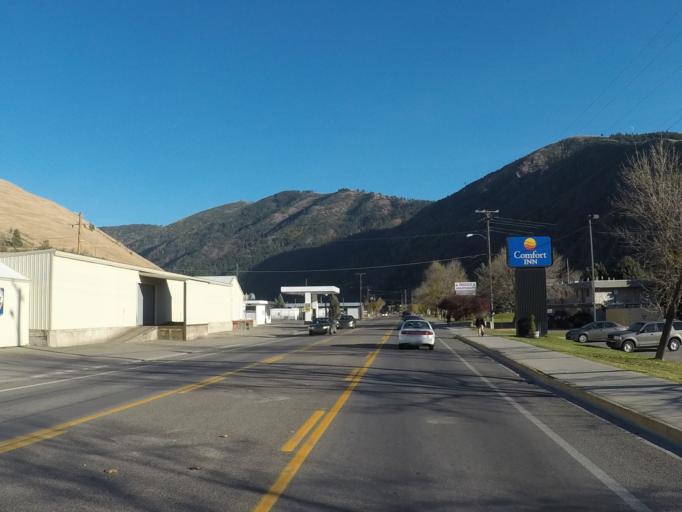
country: US
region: Montana
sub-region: Missoula County
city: Missoula
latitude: 46.8676
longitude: -113.9795
